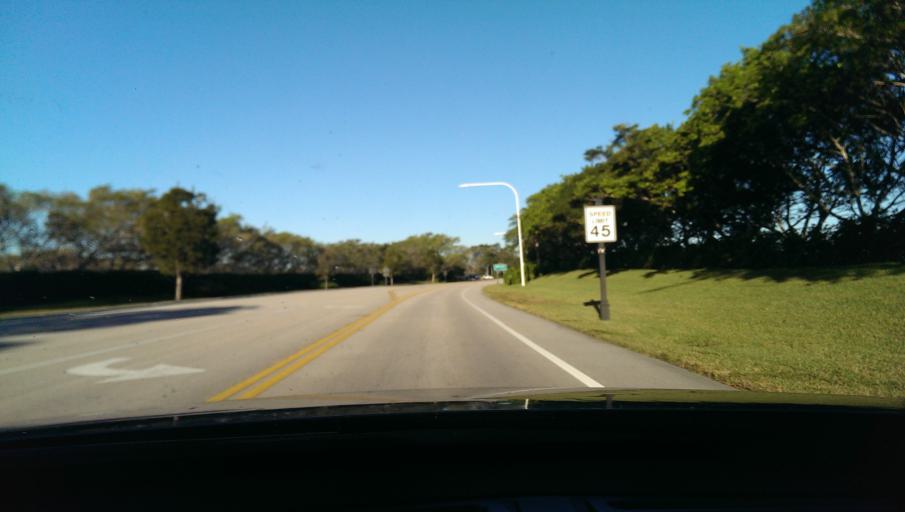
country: US
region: Florida
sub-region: Broward County
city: Weston
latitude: 26.0744
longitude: -80.3938
